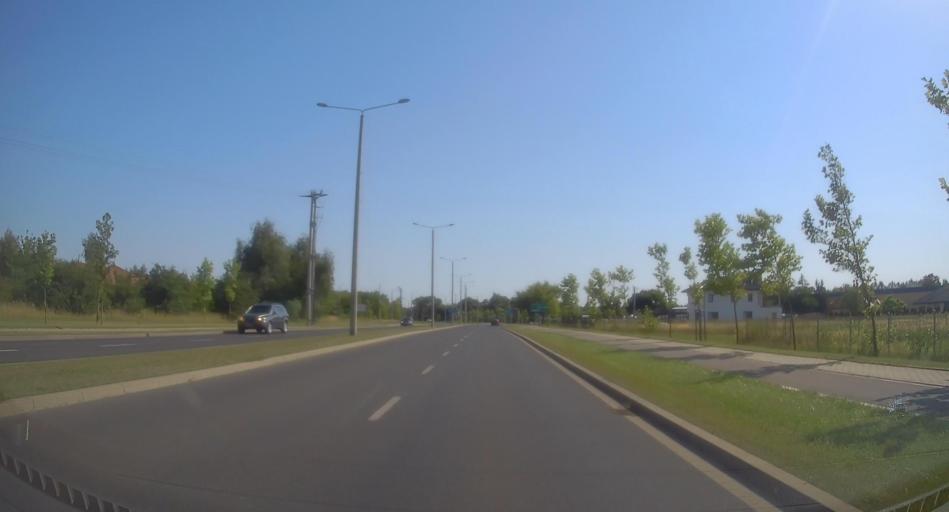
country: PL
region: Lodz Voivodeship
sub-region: Skierniewice
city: Skierniewice
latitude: 51.9457
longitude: 20.1586
